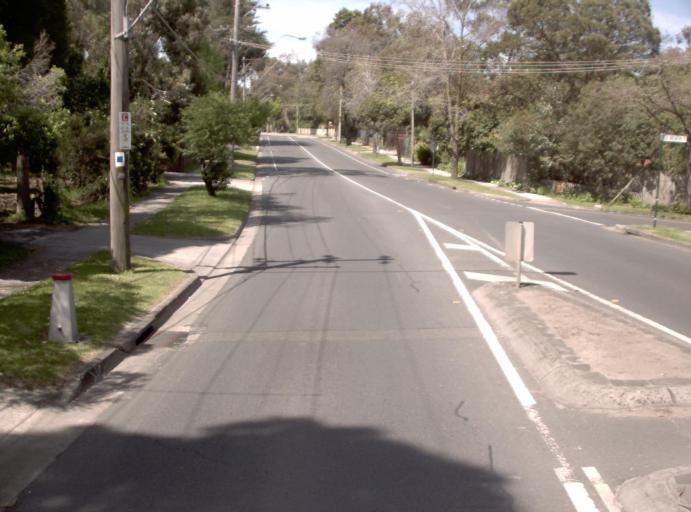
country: AU
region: Victoria
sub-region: Whitehorse
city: Blackburn
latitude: -37.8274
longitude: 145.1528
